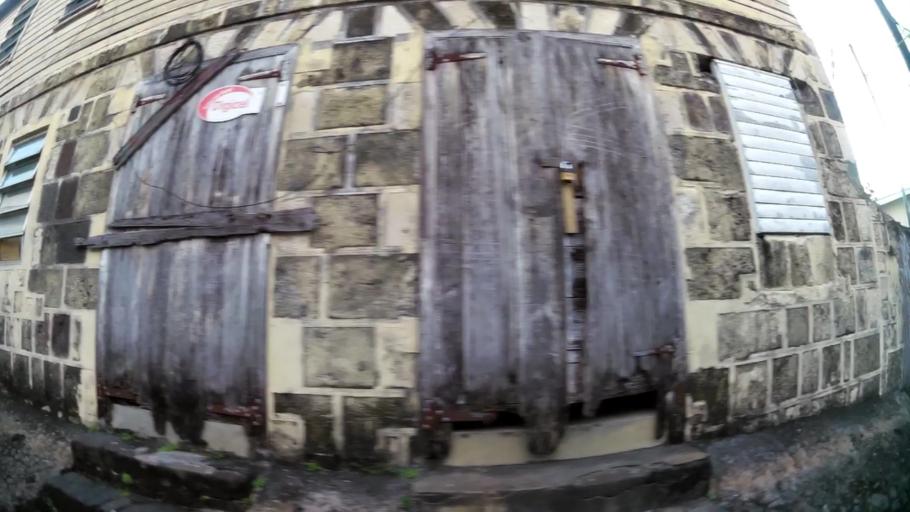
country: KN
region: Saint Anne Sandy Point
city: Sandy Point Town
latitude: 17.3625
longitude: -62.8507
